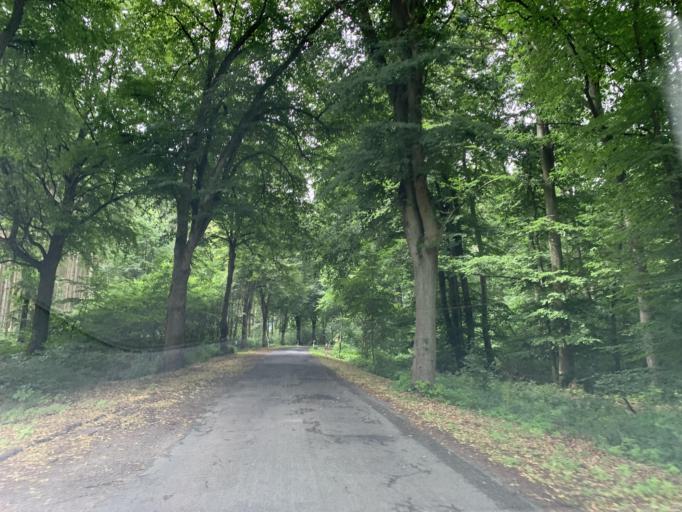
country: DE
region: Mecklenburg-Vorpommern
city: Burg Stargard
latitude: 53.4733
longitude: 13.2792
